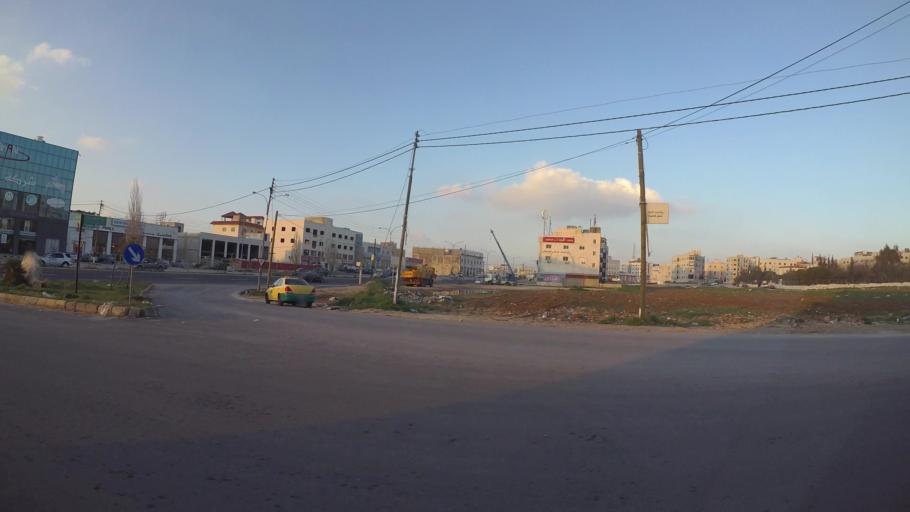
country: JO
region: Amman
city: Al Quwaysimah
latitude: 31.8985
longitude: 35.9247
